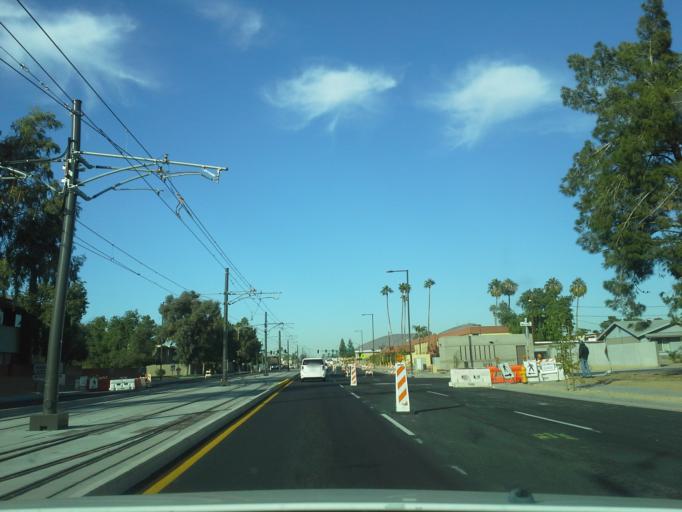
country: US
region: Arizona
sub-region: Maricopa County
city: Glendale
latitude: 33.5473
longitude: -112.0996
